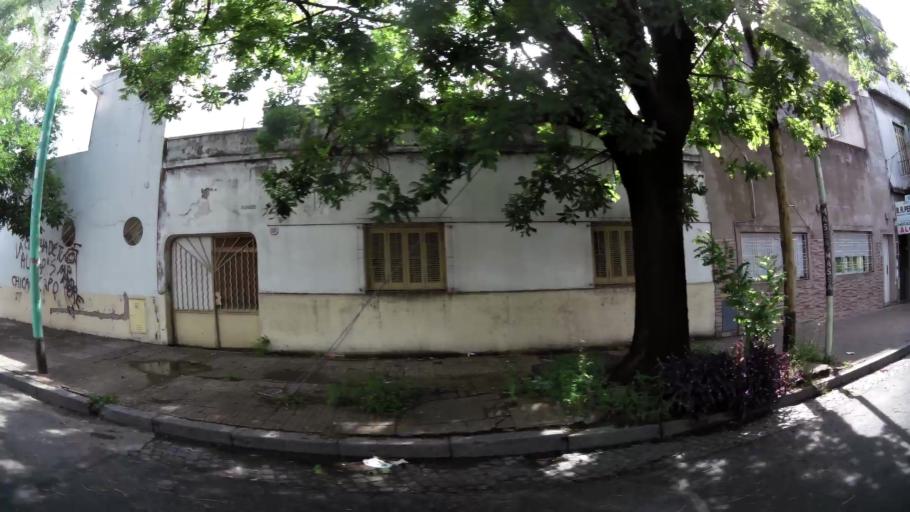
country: AR
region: Buenos Aires F.D.
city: Villa Lugano
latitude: -34.6702
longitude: -58.5000
